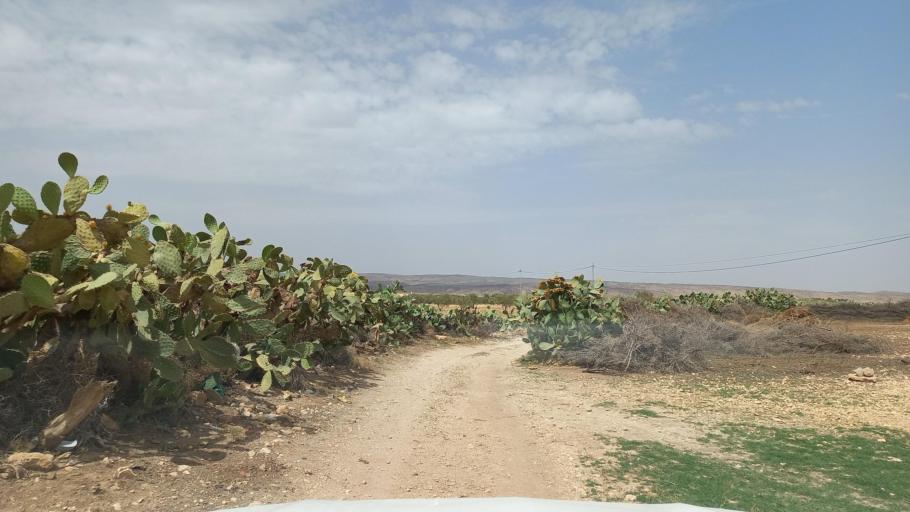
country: TN
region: Al Qasrayn
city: Kasserine
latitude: 35.2879
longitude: 9.0060
